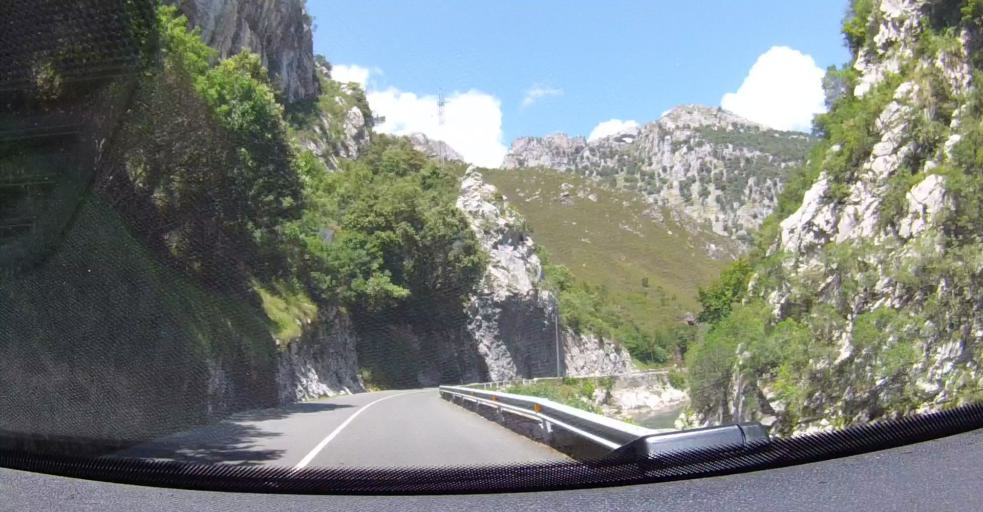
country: ES
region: Cantabria
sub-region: Provincia de Cantabria
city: Tresviso
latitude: 43.2736
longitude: -4.6369
